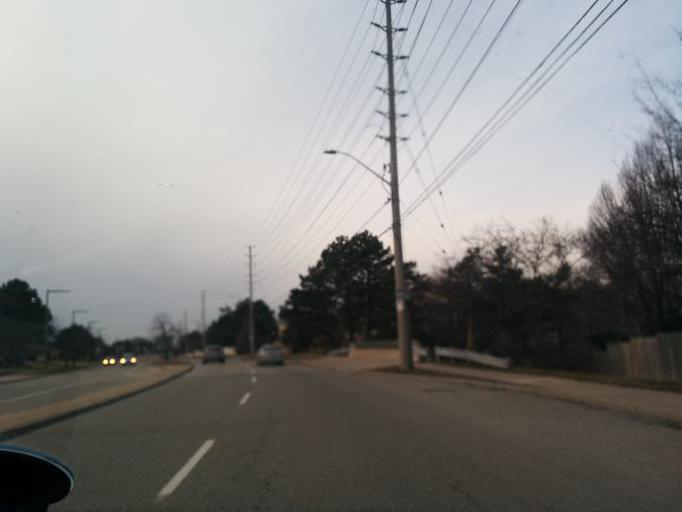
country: CA
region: Ontario
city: Mississauga
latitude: 43.5460
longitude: -79.6958
